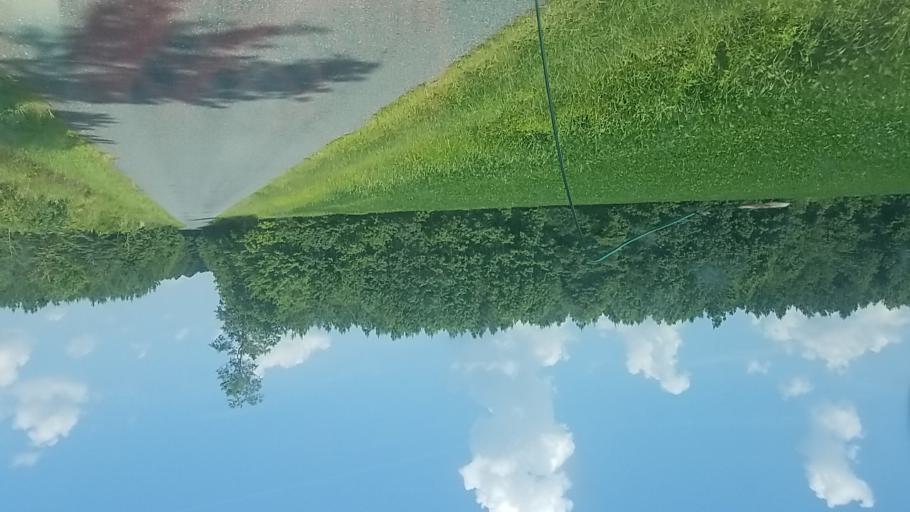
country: US
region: Maryland
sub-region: Worcester County
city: Berlin
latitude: 38.2859
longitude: -75.3058
